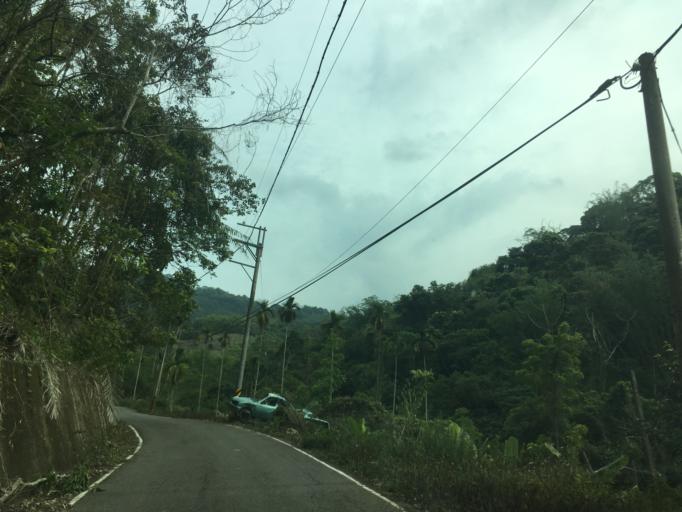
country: TW
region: Taiwan
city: Zhongxing New Village
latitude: 23.9820
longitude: 120.8158
